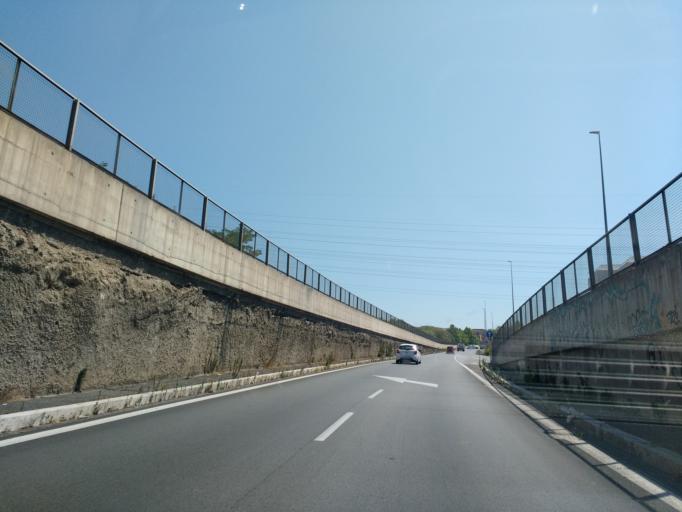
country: IT
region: Latium
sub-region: Citta metropolitana di Roma Capitale
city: Setteville
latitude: 41.9414
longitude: 12.6398
